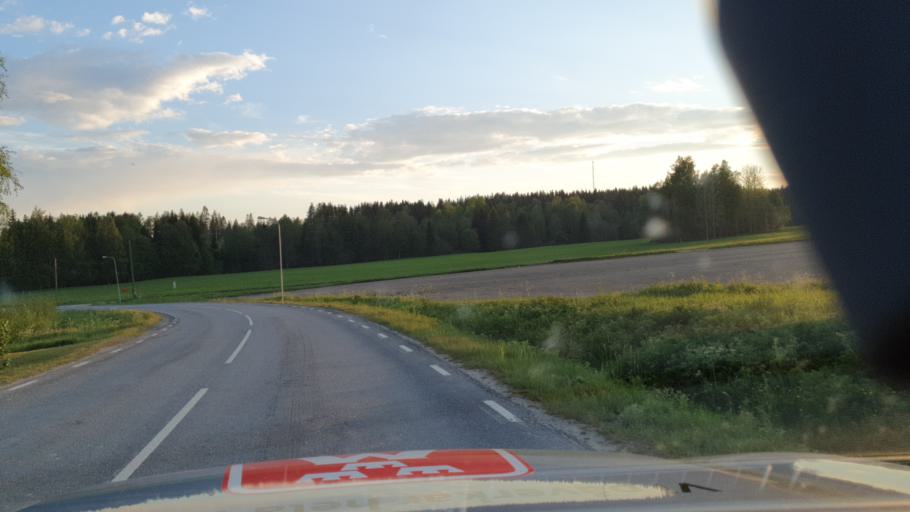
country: SE
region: Vaesternorrland
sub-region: OErnskoeldsviks Kommun
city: Kopmanholmen
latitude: 63.2325
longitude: 18.5664
